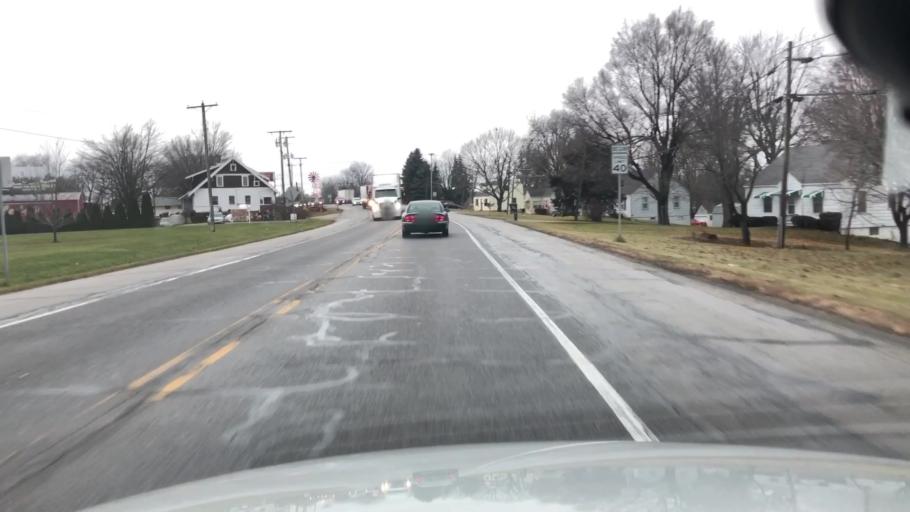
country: US
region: Indiana
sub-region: Allen County
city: New Haven
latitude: 41.0663
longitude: -85.0040
